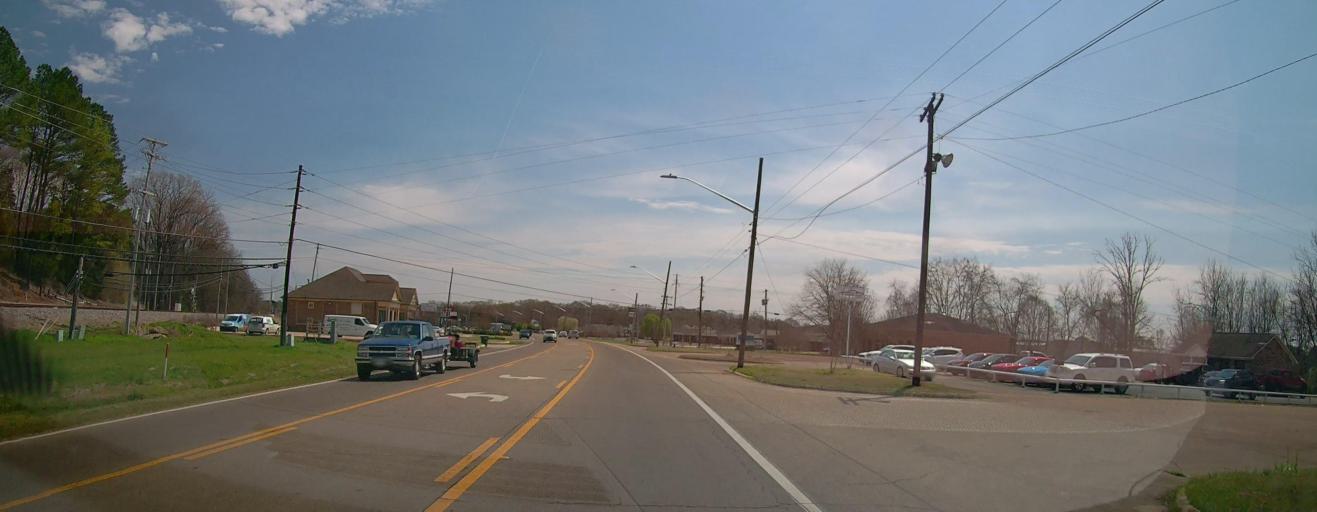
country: US
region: Mississippi
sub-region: Union County
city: New Albany
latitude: 34.4978
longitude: -89.0224
